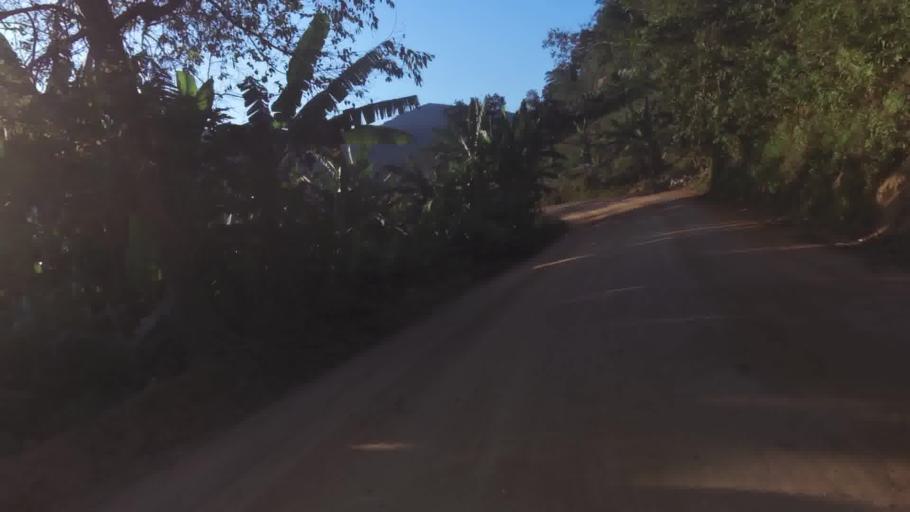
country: BR
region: Espirito Santo
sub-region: Alfredo Chaves
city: Alfredo Chaves
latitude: -20.5962
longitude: -40.6961
